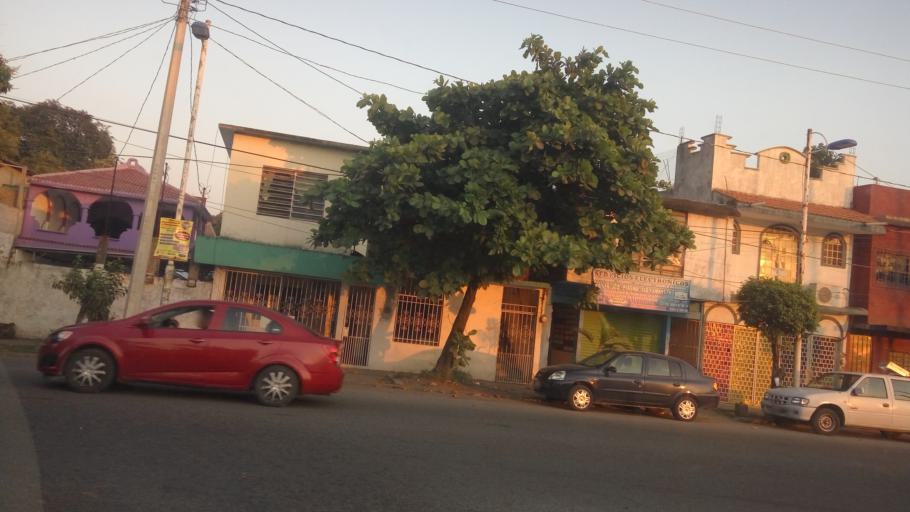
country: MX
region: Tabasco
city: Villahermosa
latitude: 17.9820
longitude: -92.9208
